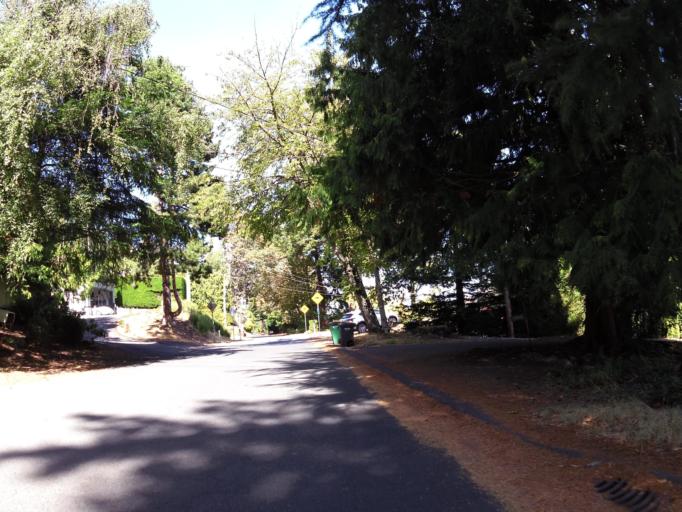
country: CA
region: British Columbia
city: Victoria
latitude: 48.5128
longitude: -123.3667
